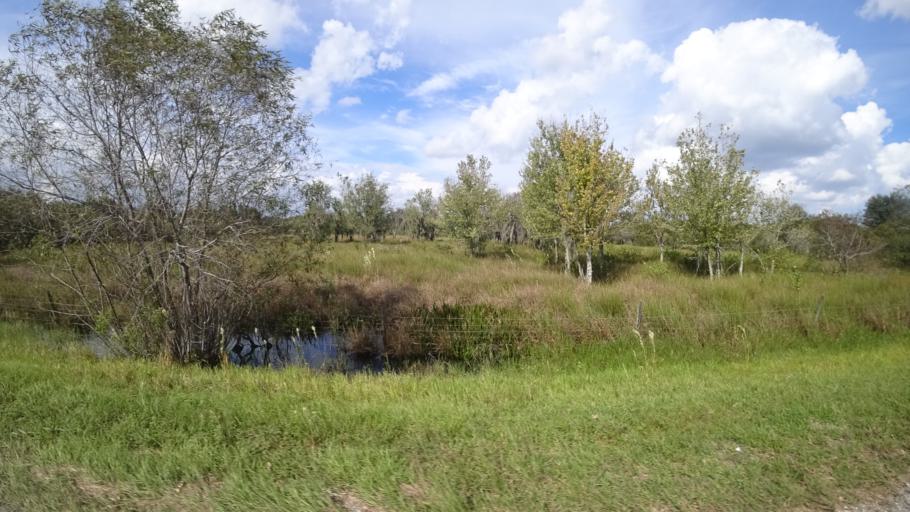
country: US
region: Florida
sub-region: Hardee County
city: Wauchula
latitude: 27.5373
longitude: -82.0825
